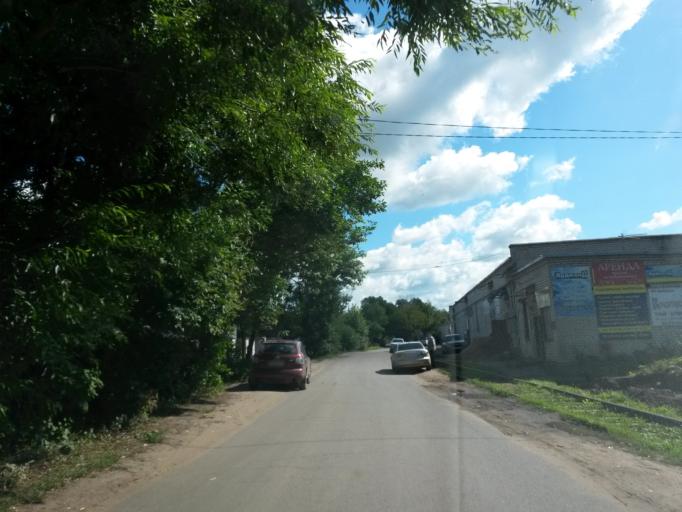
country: RU
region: Jaroslavl
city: Yaroslavl
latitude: 57.6033
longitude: 39.8844
